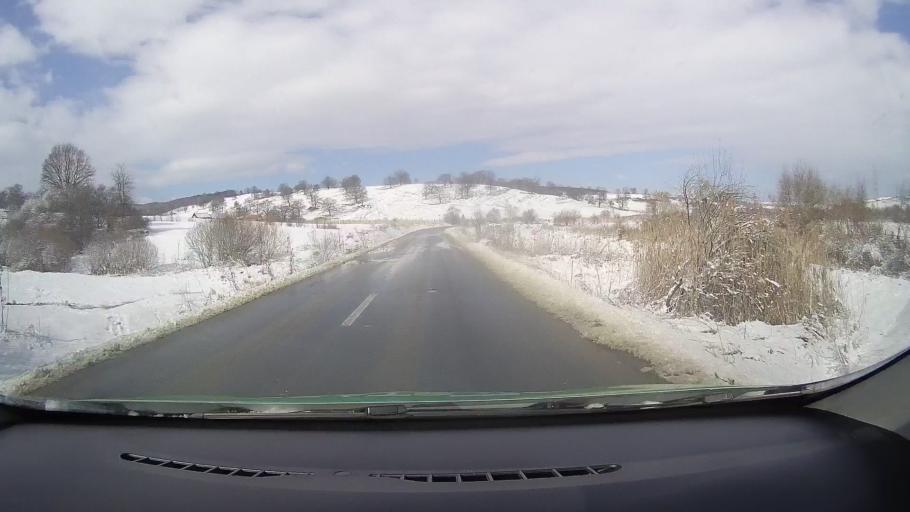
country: RO
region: Sibiu
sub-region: Comuna Altina
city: Altina
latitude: 45.9456
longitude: 24.4514
